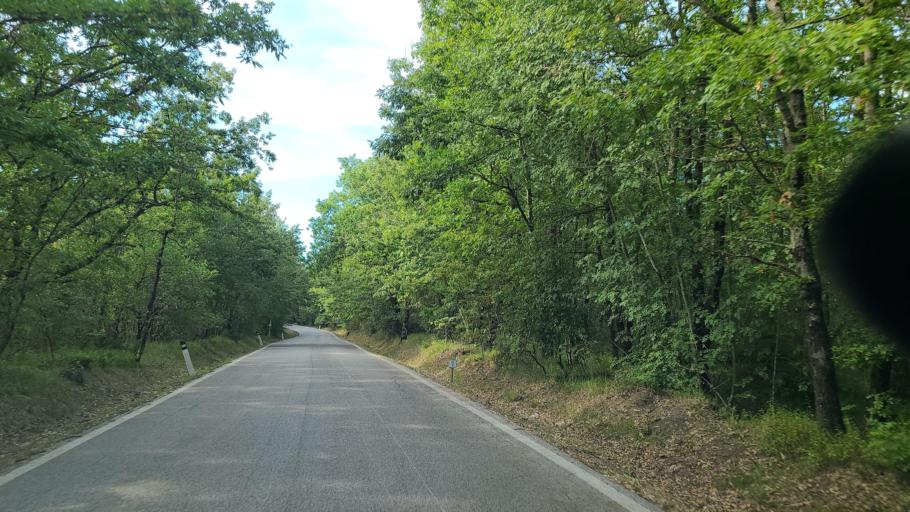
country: IT
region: Tuscany
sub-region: Provincia di Siena
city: San Gimignano
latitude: 43.4329
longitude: 10.9679
